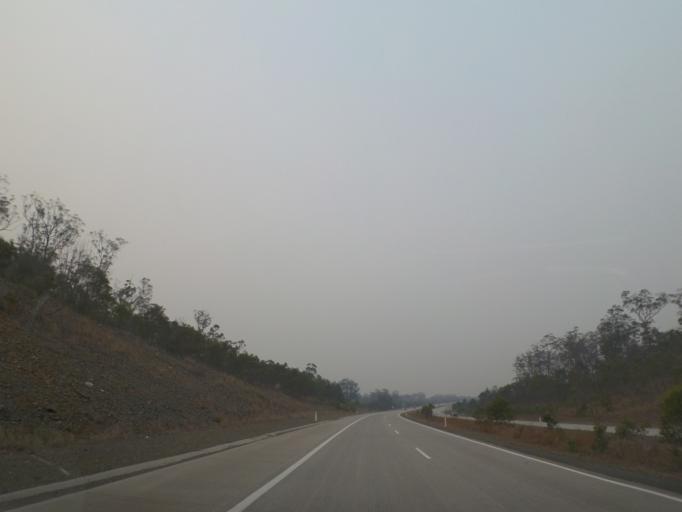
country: AU
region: New South Wales
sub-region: Kempsey
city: Kempsey
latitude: -31.1147
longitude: 152.8328
